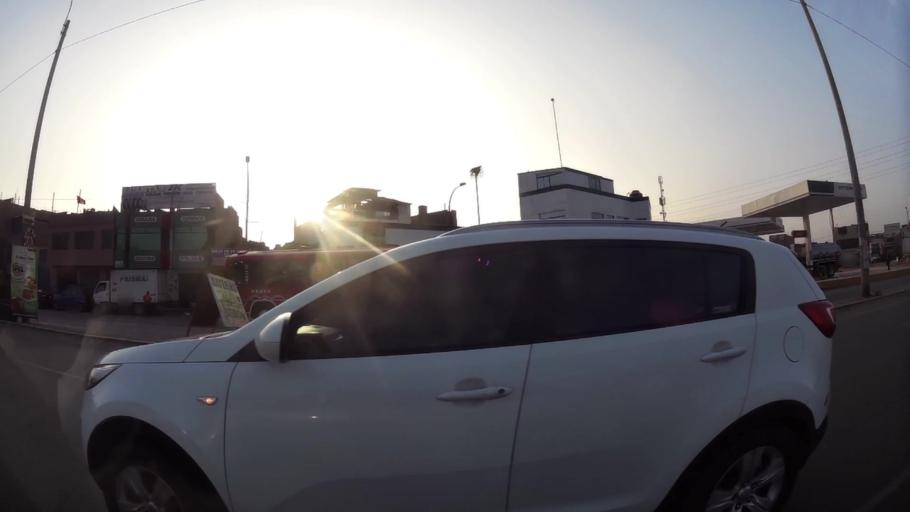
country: PE
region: Lima
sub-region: Lima
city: Independencia
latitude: -11.9897
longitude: -77.1064
